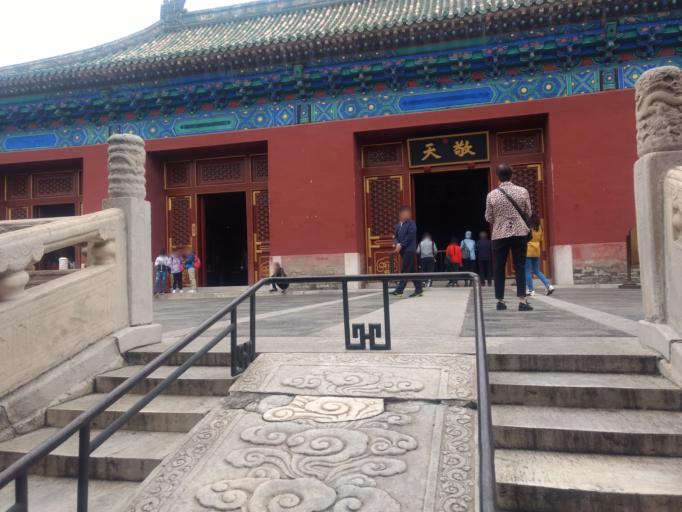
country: CN
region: Beijing
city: Longtan
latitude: 39.8784
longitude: 116.4007
